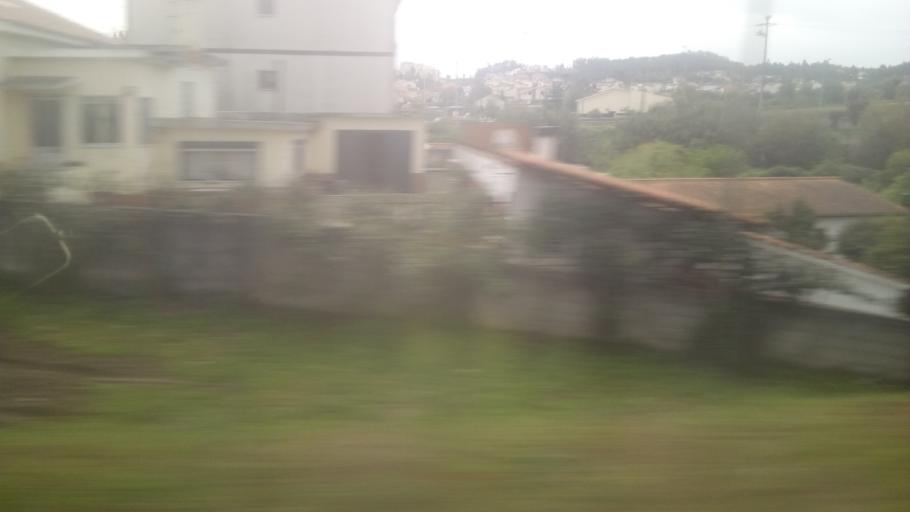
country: PT
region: Coimbra
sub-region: Coimbra
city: Coimbra
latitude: 40.2089
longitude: -8.4714
